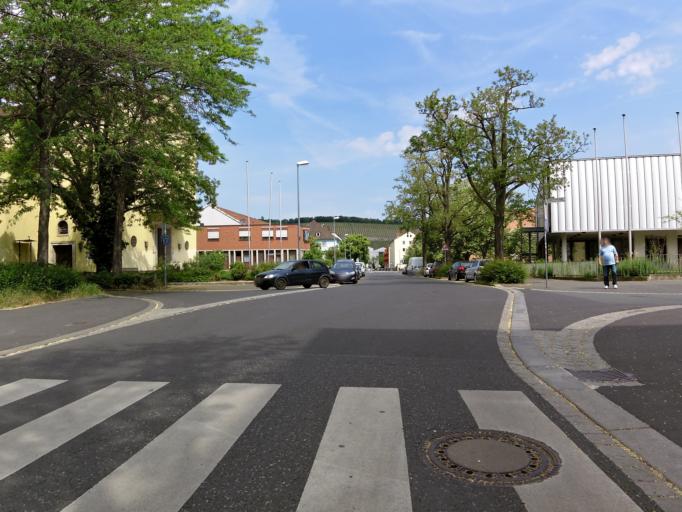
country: DE
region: Bavaria
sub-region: Regierungsbezirk Unterfranken
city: Hochberg
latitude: 49.7966
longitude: 9.9114
